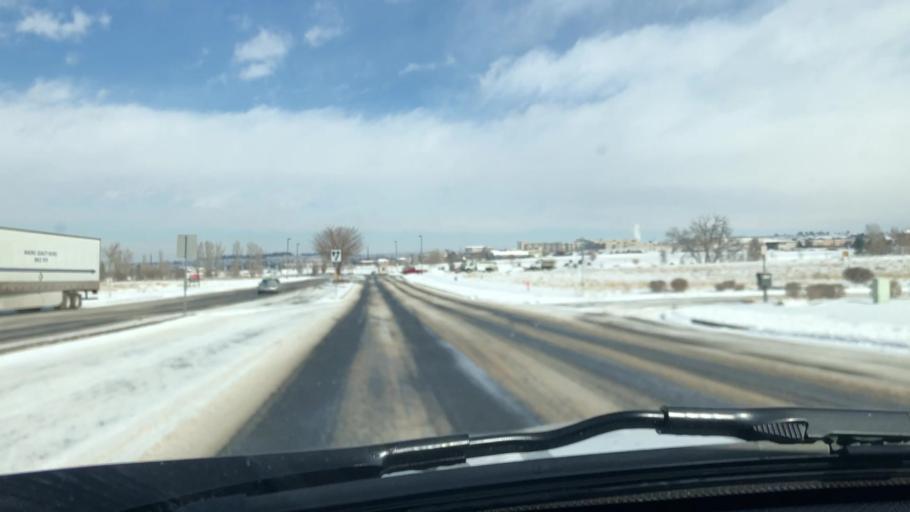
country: US
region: Colorado
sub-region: Douglas County
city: Parker
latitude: 39.5382
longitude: -104.7746
